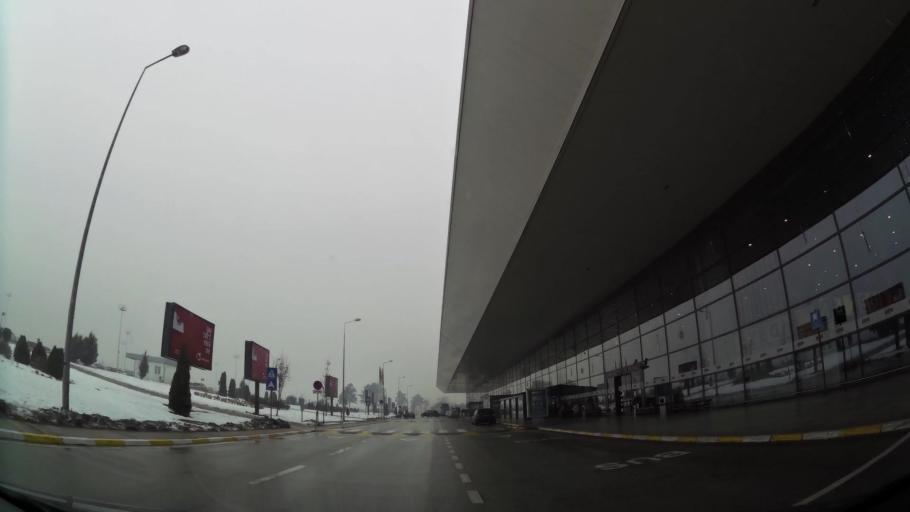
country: MK
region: Petrovec
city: Petrovec
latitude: 41.9615
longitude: 21.6275
